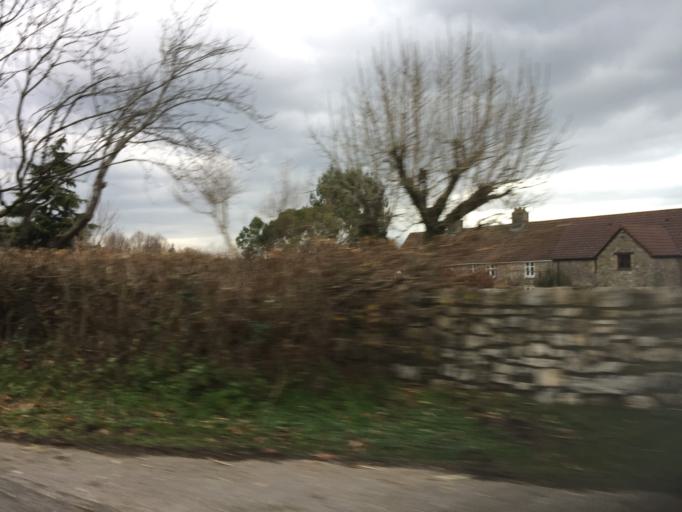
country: GB
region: Wales
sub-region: Monmouthshire
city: Chepstow
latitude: 51.6036
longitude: -2.7098
